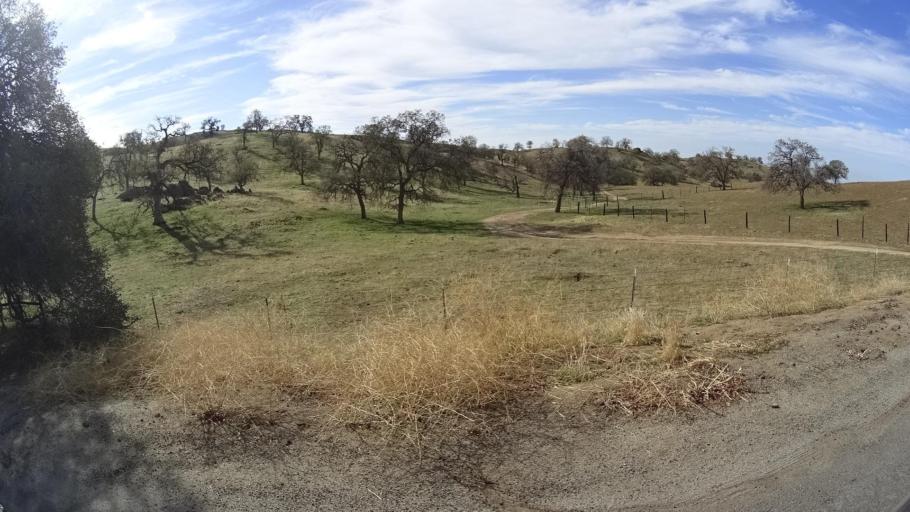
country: US
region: California
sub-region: Kern County
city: Oildale
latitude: 35.6092
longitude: -118.8355
